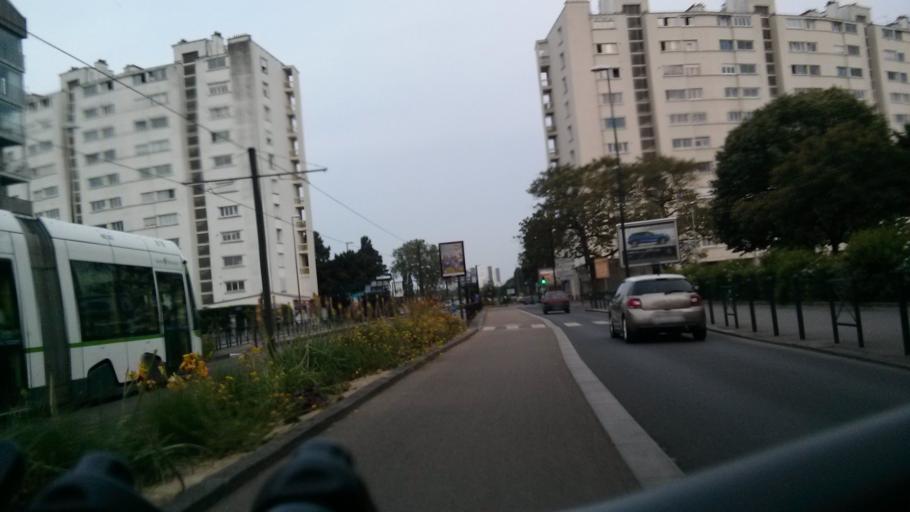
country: FR
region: Pays de la Loire
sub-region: Departement de la Loire-Atlantique
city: Nantes
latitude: 47.2025
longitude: -1.5456
